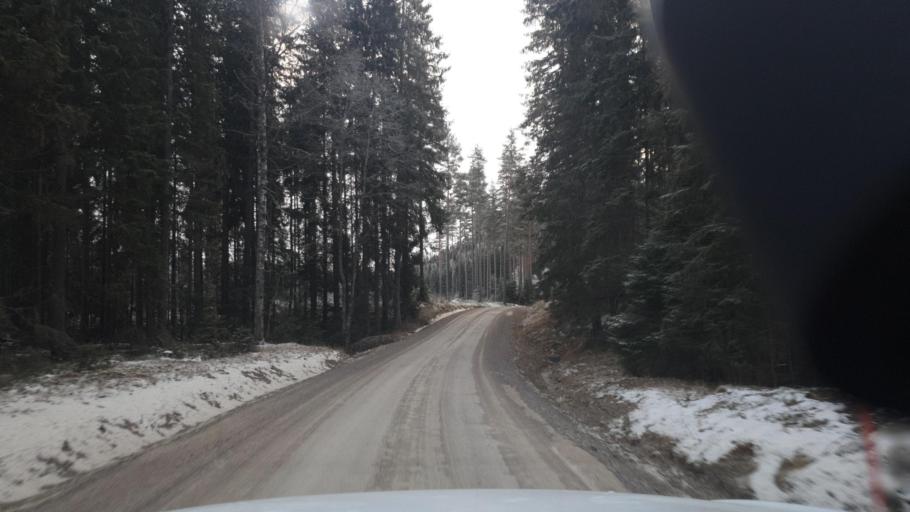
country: SE
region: Vaermland
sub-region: Eda Kommun
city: Charlottenberg
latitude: 60.0349
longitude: 12.5959
